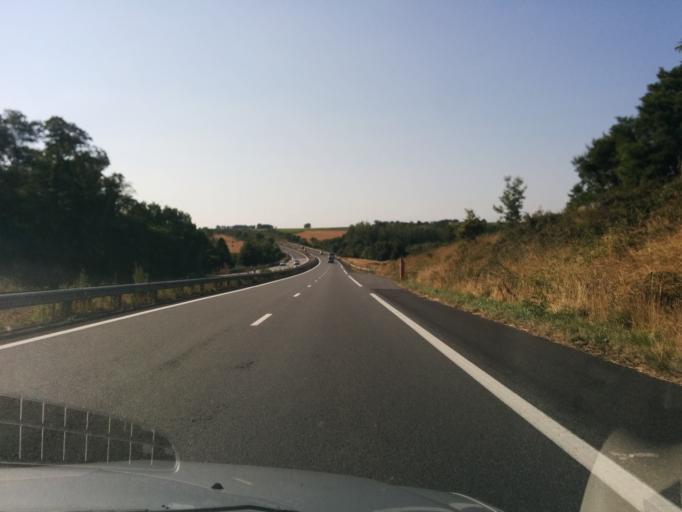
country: FR
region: Pays de la Loire
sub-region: Departement de Maine-et-Loire
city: Tillieres
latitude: 47.1491
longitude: -1.1944
